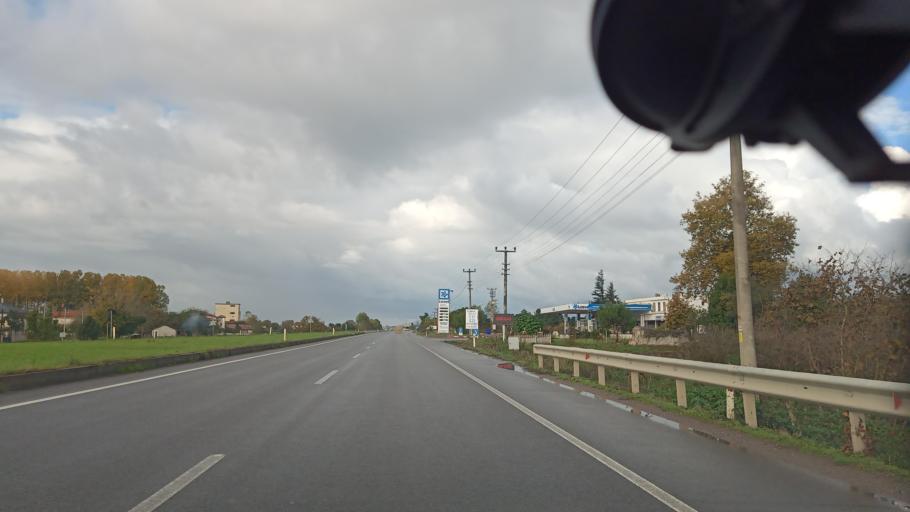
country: TR
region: Sakarya
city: Karasu
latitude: 41.0759
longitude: 30.7824
